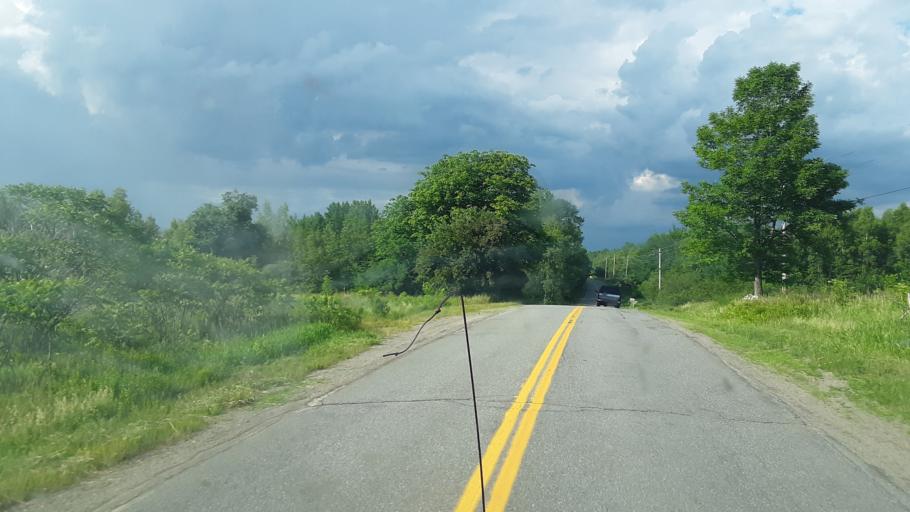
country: US
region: Maine
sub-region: Washington County
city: Calais
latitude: 45.1021
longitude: -67.5111
